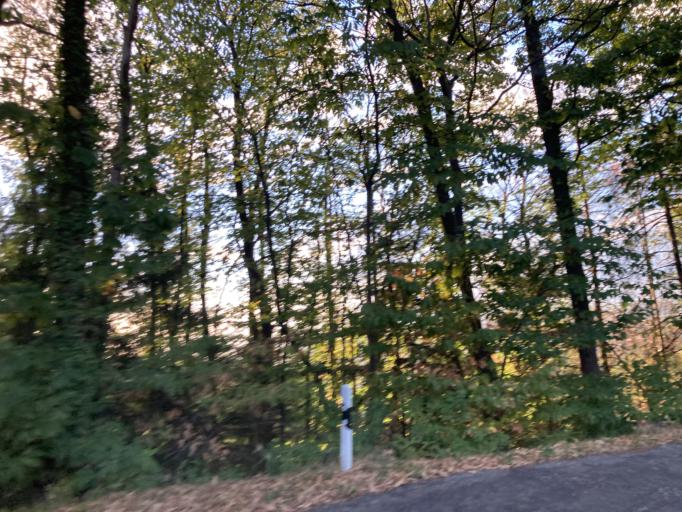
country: DE
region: Baden-Wuerttemberg
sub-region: Freiburg Region
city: Lauf
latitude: 48.6706
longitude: 8.1547
